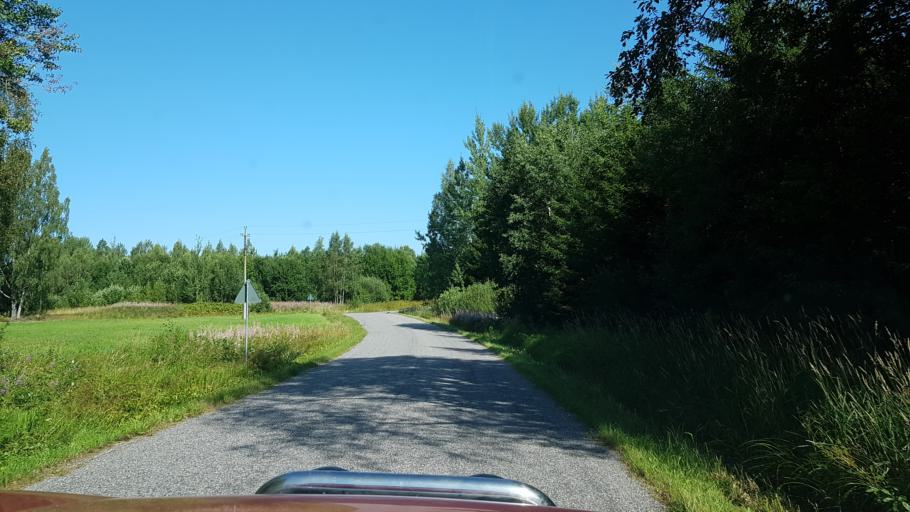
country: EE
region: Vorumaa
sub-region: Voru linn
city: Voru
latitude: 57.7070
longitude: 27.1905
